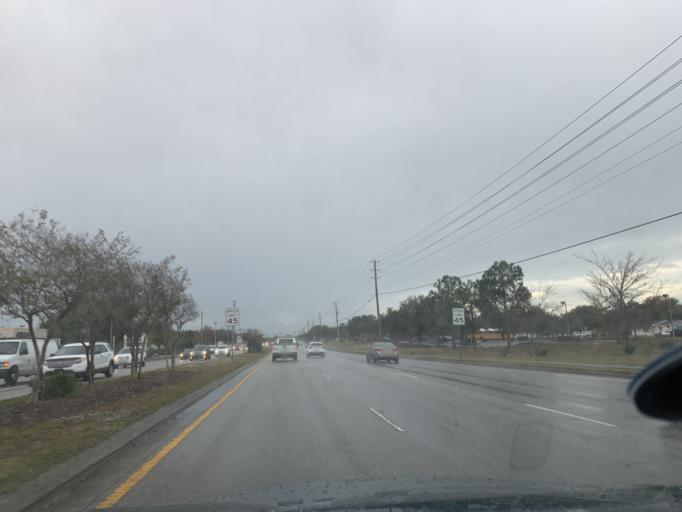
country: US
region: Florida
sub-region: Pasco County
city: Jasmine Estates
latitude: 28.2995
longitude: -82.6711
